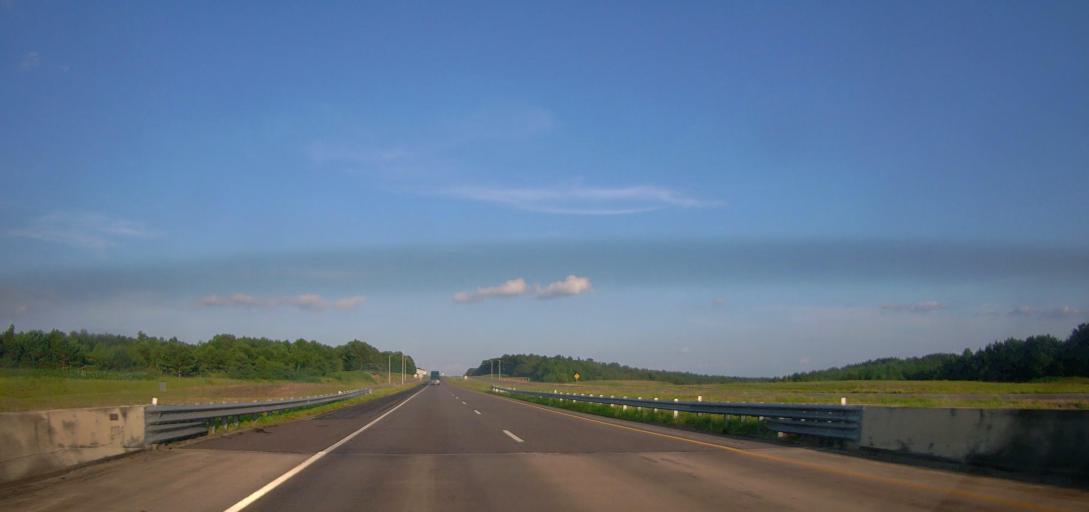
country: US
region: Alabama
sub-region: Walker County
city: Carbon Hill
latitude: 33.9112
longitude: -87.5027
